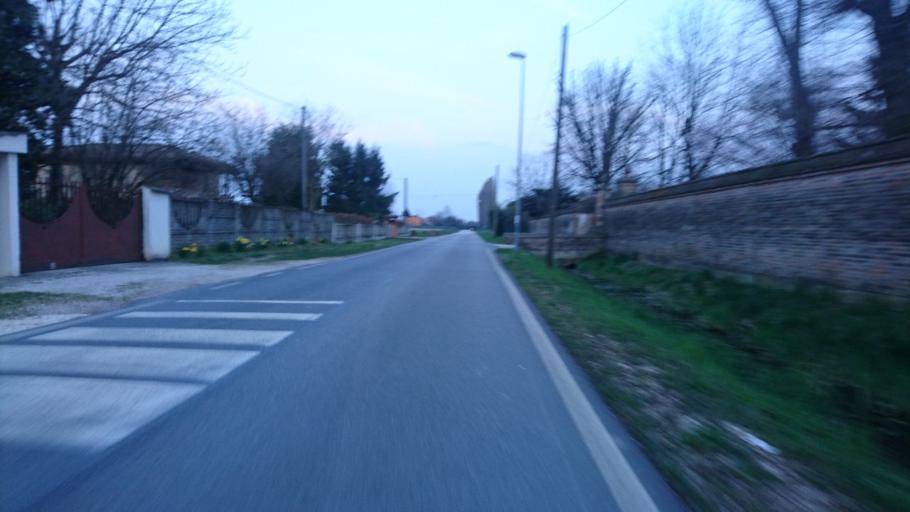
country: IT
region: Veneto
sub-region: Provincia di Padova
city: Saccolongo
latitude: 45.3910
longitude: 11.7527
